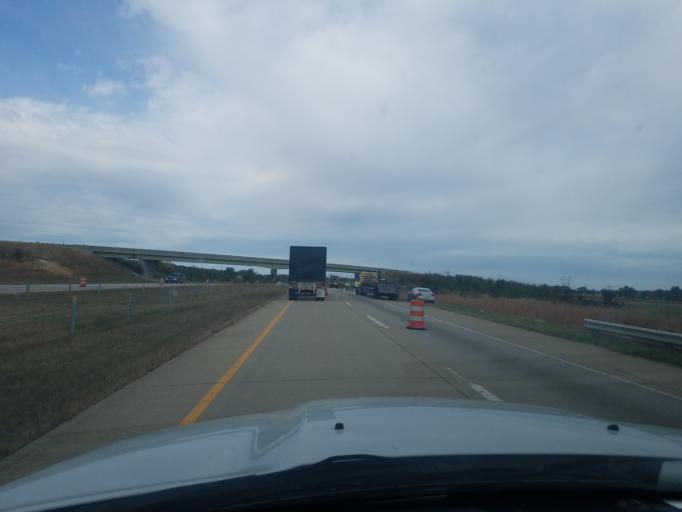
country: US
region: Indiana
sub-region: Vanderburgh County
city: Darmstadt
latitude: 38.1371
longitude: -87.4728
